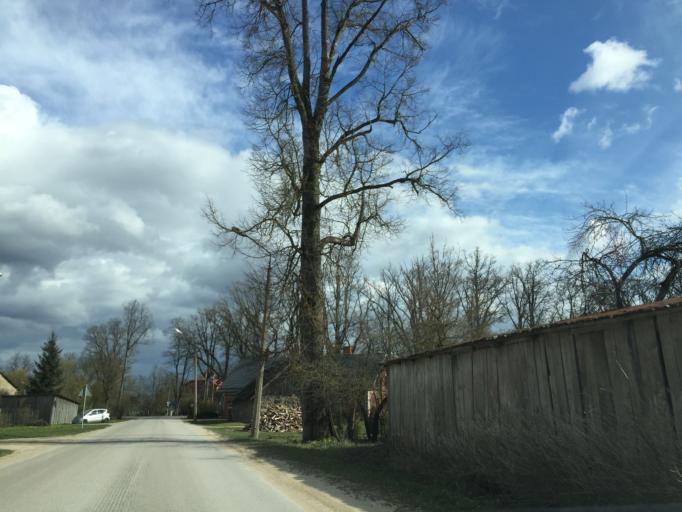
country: LV
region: Burtnieki
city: Matisi
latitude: 57.5983
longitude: 25.0930
